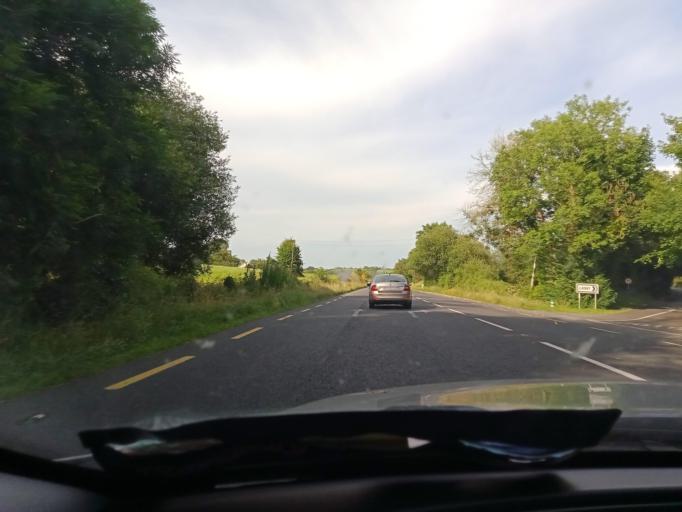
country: IE
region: Ulster
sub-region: An Cabhan
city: Cavan
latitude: 53.9428
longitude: -7.3862
